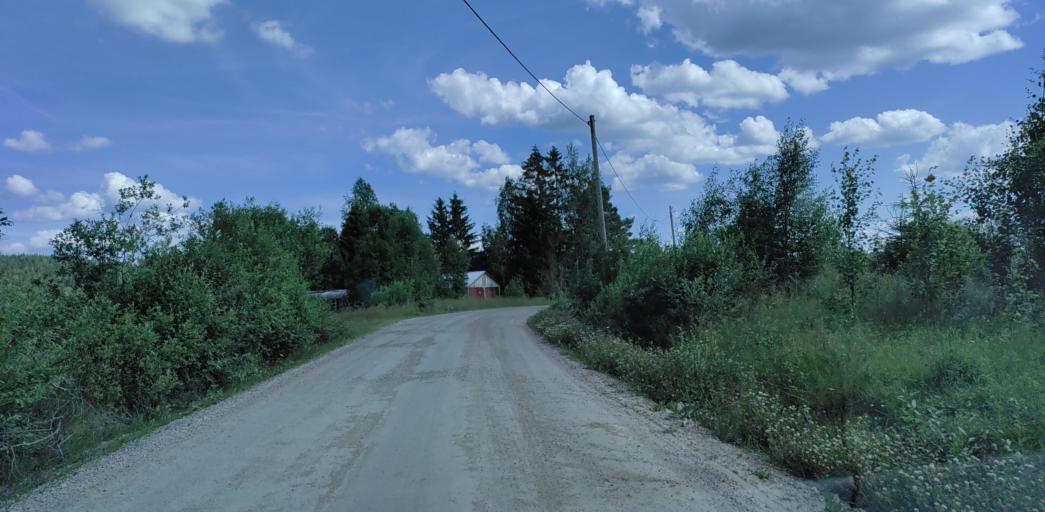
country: SE
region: Vaermland
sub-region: Hagfors Kommun
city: Ekshaerad
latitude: 60.1272
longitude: 13.4748
